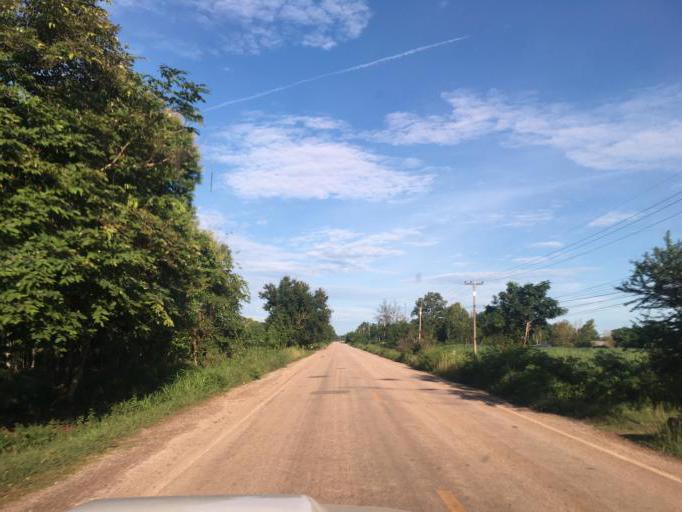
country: TH
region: Changwat Udon Thani
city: Kut Chap
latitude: 17.3836
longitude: 102.6193
